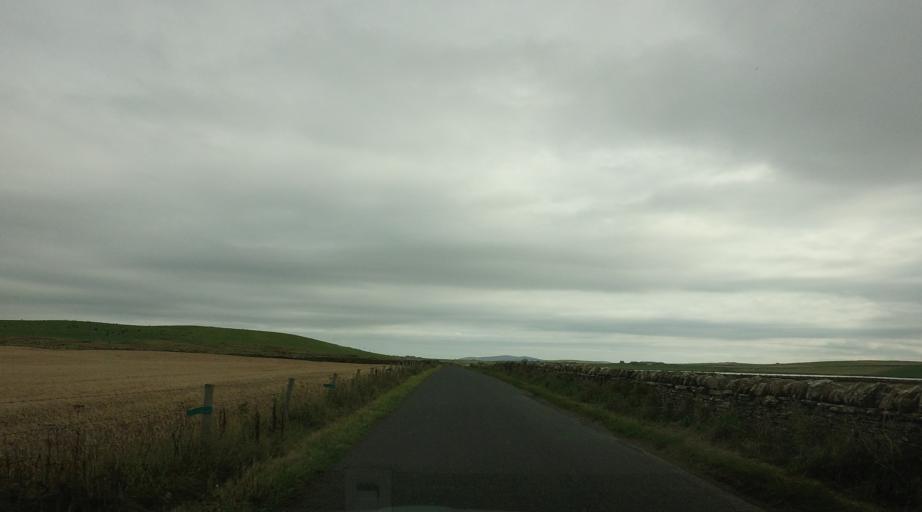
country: GB
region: Scotland
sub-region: Orkney Islands
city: Stromness
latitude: 59.0493
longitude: -3.3304
